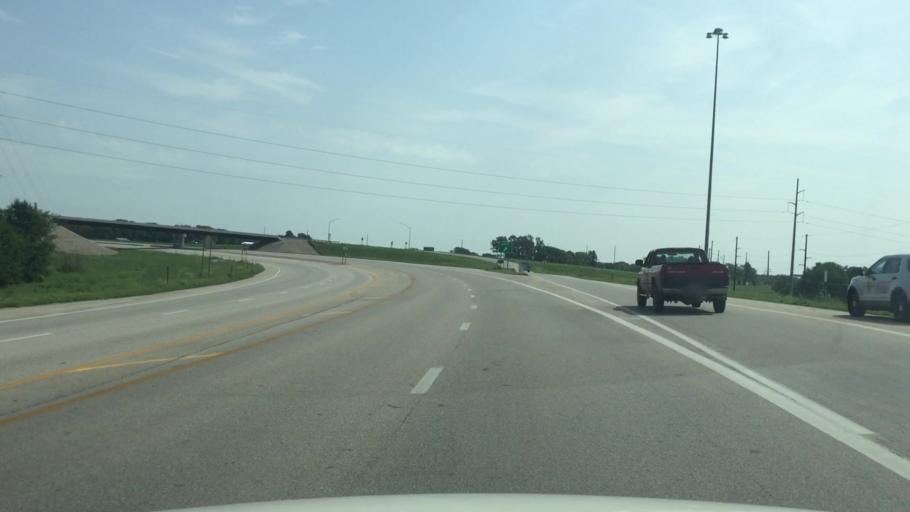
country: US
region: Kansas
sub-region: Montgomery County
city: Coffeyville
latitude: 37.0438
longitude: -95.5853
